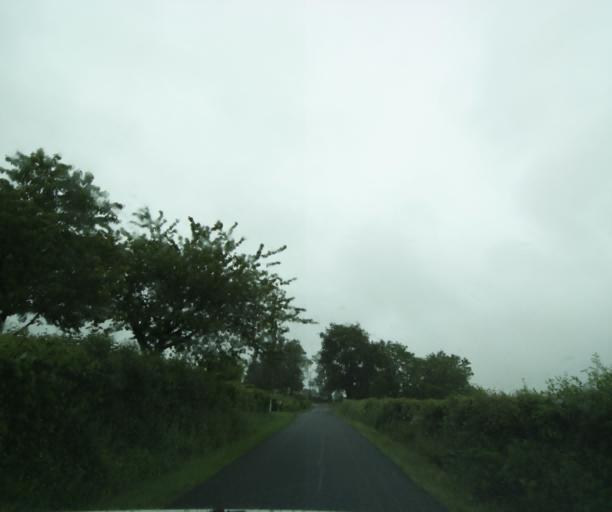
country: FR
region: Bourgogne
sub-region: Departement de Saone-et-Loire
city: Charolles
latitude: 46.4122
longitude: 4.2377
